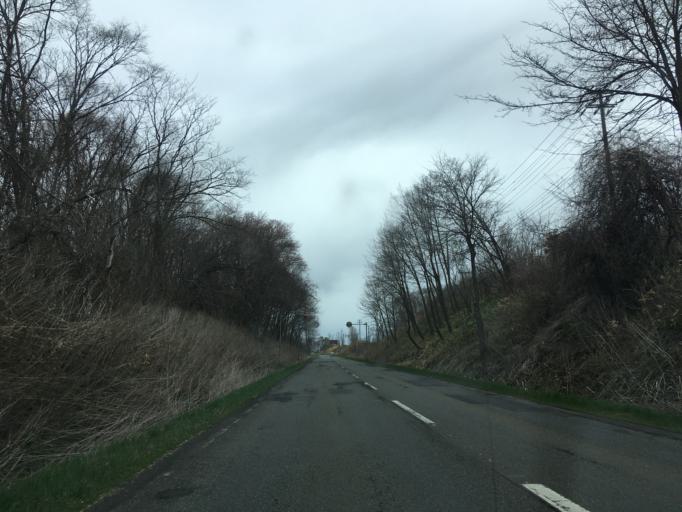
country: JP
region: Hokkaido
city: Chitose
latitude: 42.8943
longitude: 141.8133
